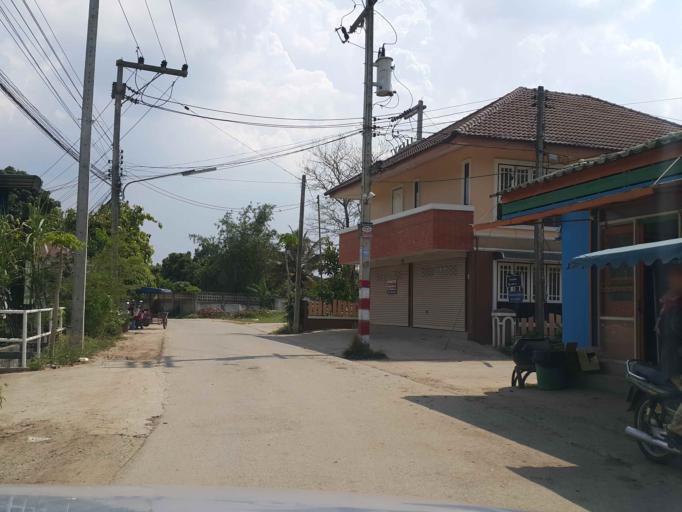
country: TH
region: Chiang Mai
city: Hang Dong
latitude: 18.7017
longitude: 98.9500
